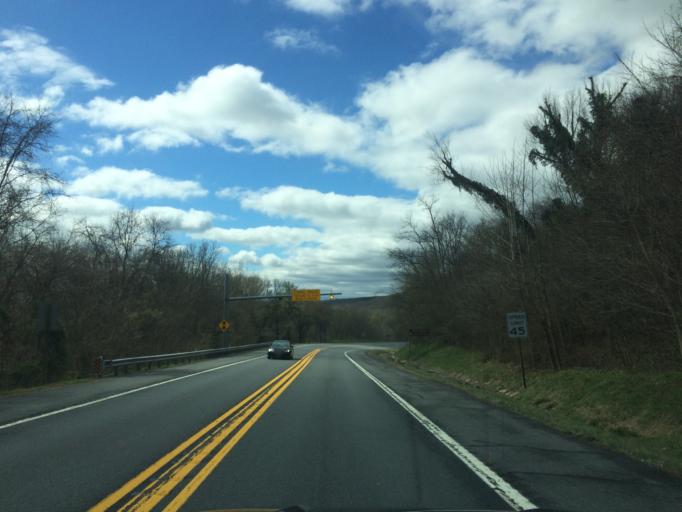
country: US
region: Maryland
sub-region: Frederick County
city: Point of Rocks
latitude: 39.2774
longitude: -77.5403
